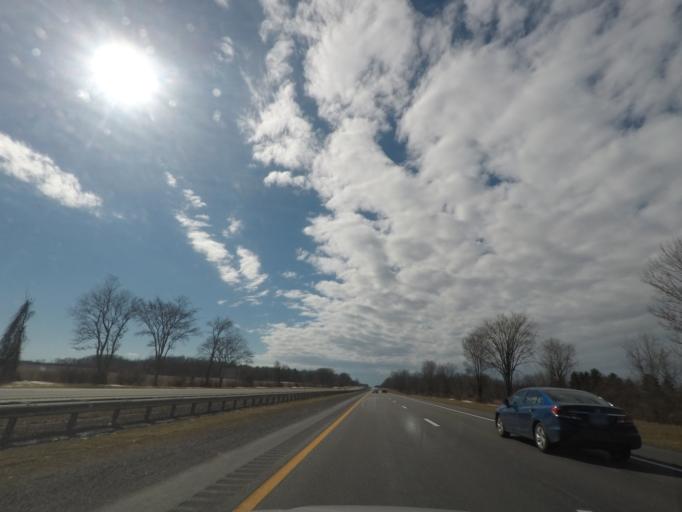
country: US
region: New York
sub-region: Oneida County
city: Vernon
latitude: 43.1317
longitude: -75.5212
